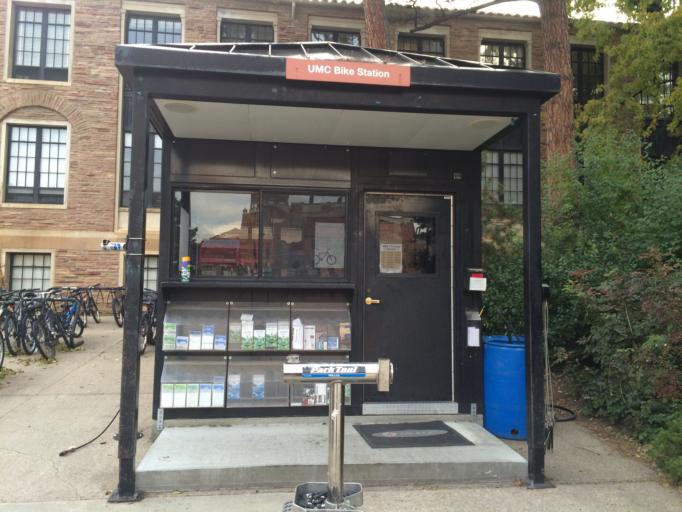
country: US
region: Colorado
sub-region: Boulder County
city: Boulder
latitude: 40.0074
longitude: -105.2721
